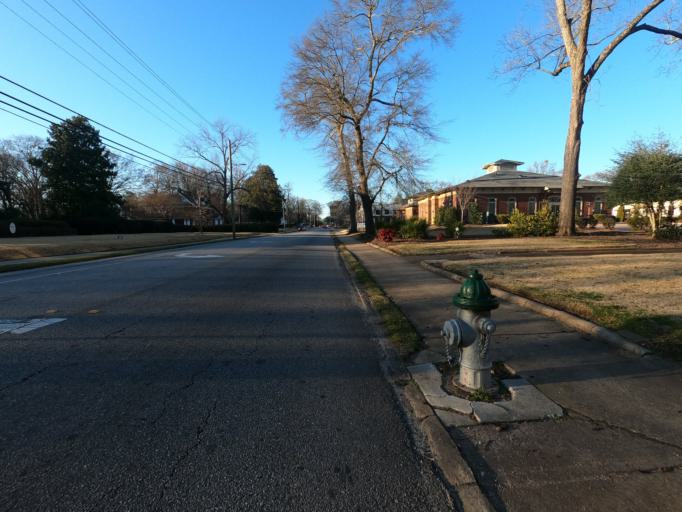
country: US
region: Georgia
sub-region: Clarke County
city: Athens
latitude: 33.9572
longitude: -83.3891
